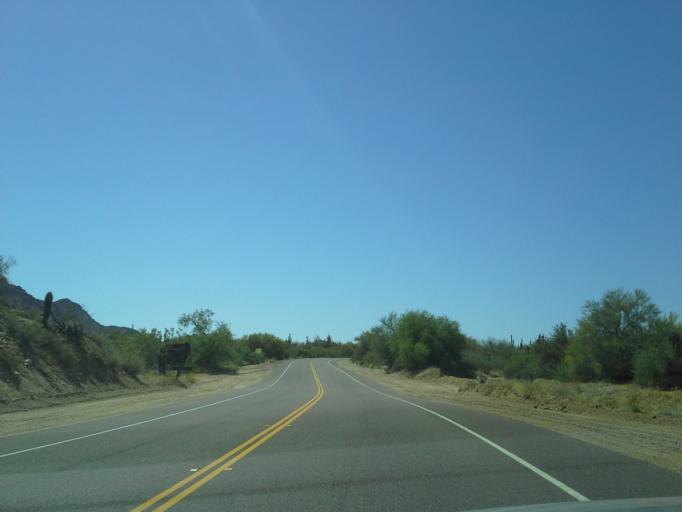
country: US
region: Arizona
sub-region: Pinal County
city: Apache Junction
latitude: 33.5014
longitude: -111.6181
